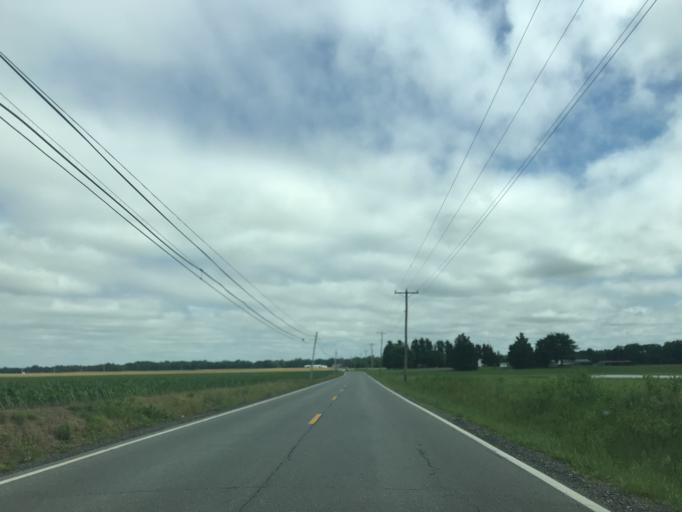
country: US
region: Maryland
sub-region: Caroline County
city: Ridgely
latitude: 38.8992
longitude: -75.9591
